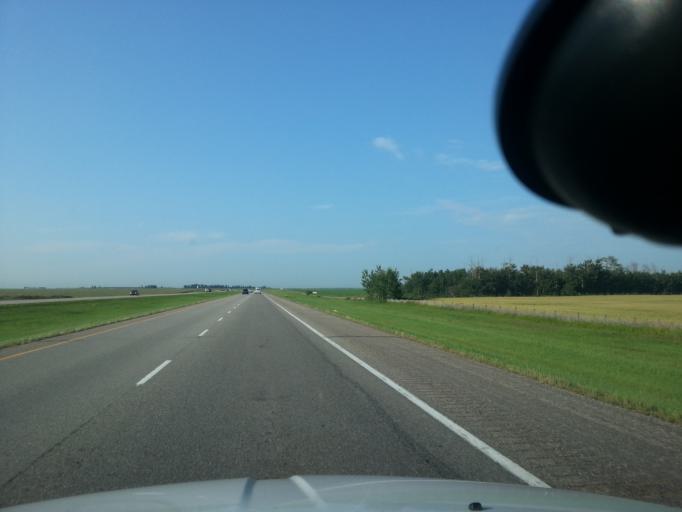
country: CA
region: Alberta
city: Leduc
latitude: 53.2080
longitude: -113.5915
